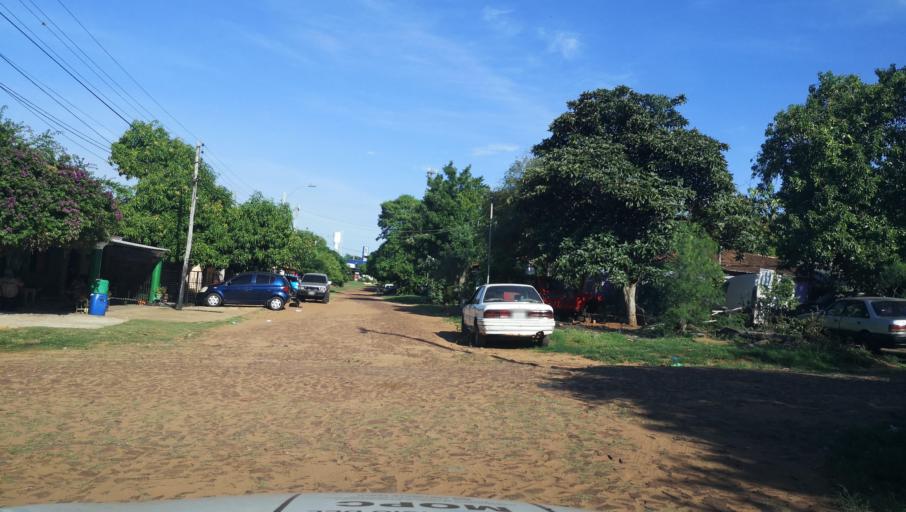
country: PY
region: Misiones
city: Santa Maria
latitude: -26.8812
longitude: -57.0085
